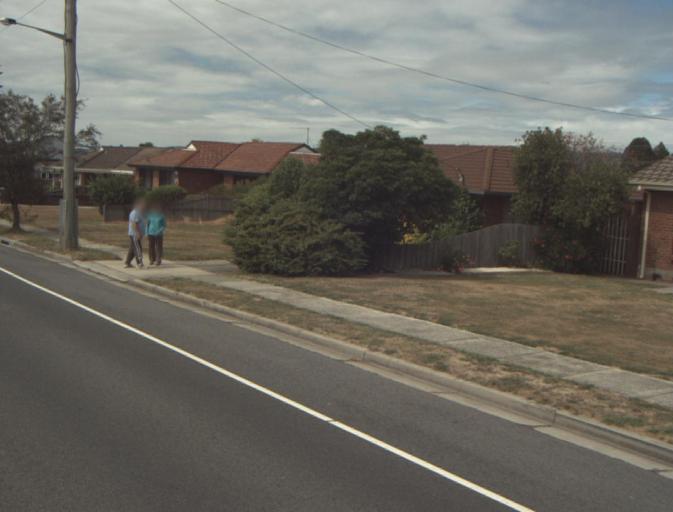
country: AU
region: Tasmania
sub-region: Launceston
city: Invermay
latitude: -41.3902
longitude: 147.1196
